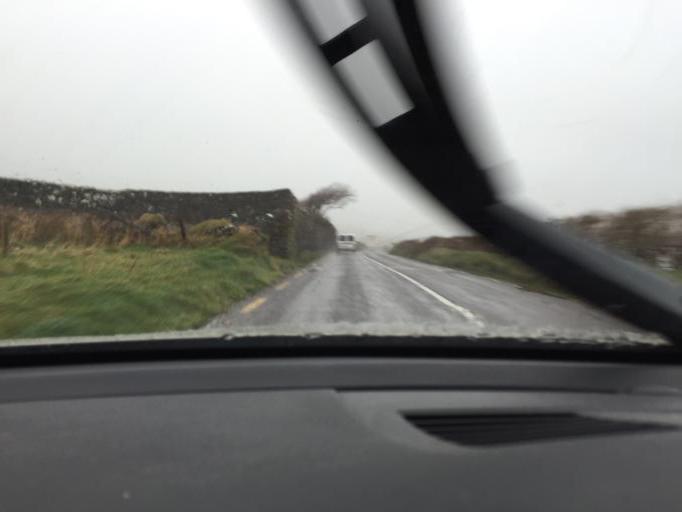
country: IE
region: Munster
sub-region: Ciarrai
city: Dingle
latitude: 52.1308
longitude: -10.2449
